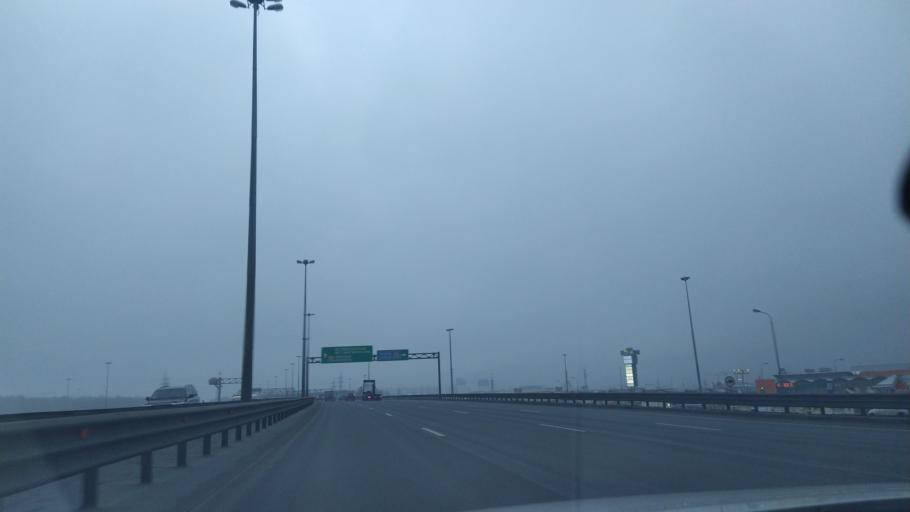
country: RU
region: Leningrad
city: Rybatskoye
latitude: 59.8963
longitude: 30.5245
